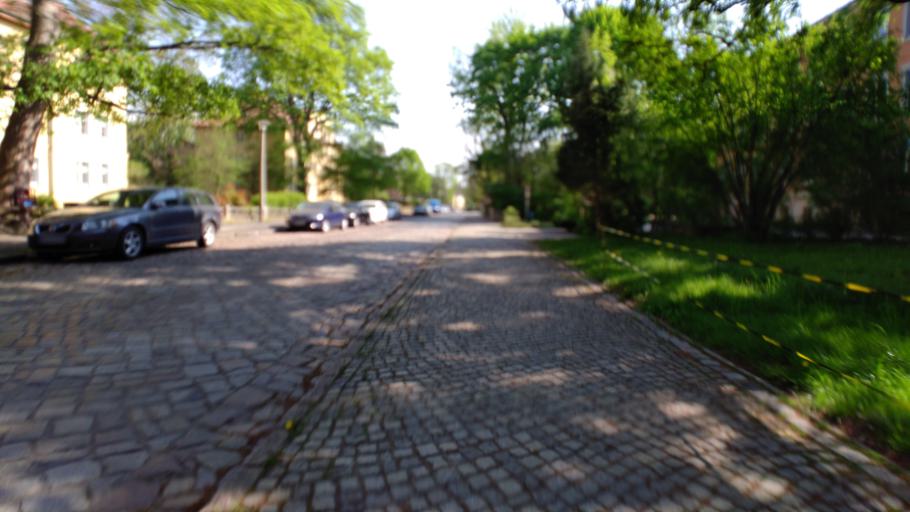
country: DE
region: Saxony
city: Albertstadt
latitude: 51.0722
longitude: 13.7653
